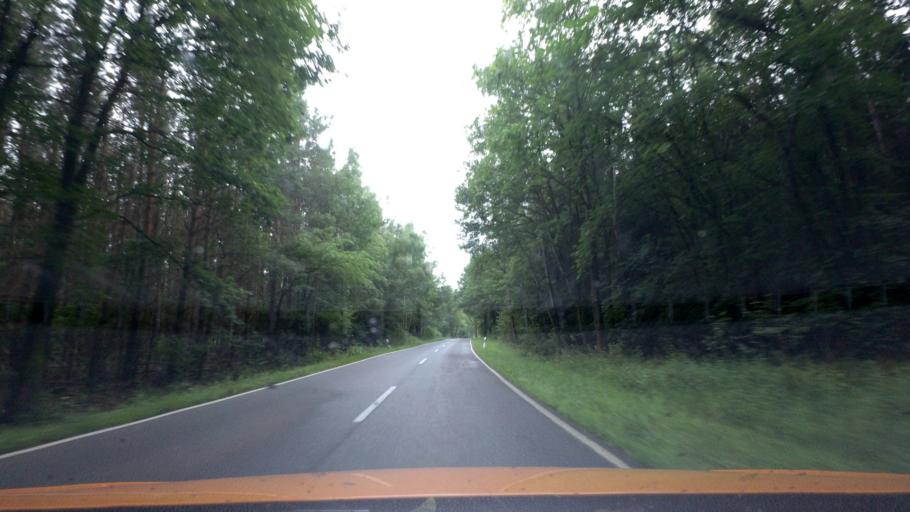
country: DE
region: Brandenburg
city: Werftpfuhl
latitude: 52.6379
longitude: 13.8546
